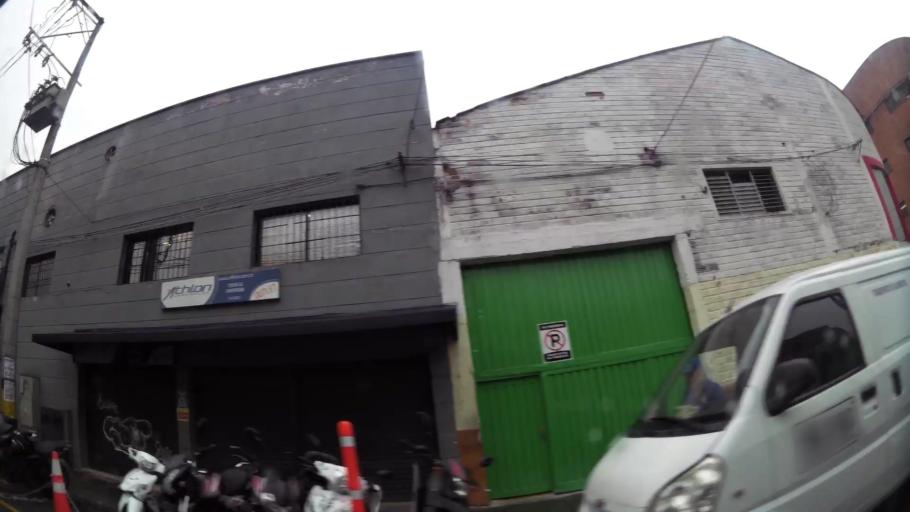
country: CO
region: Antioquia
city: Medellin
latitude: 6.2311
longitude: -75.5726
